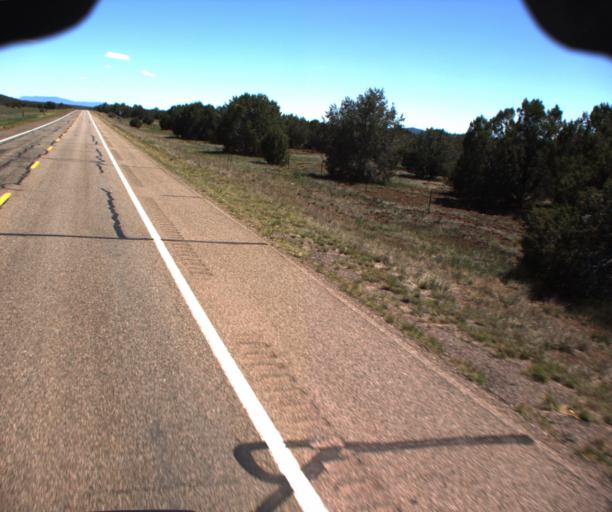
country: US
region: Arizona
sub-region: Yavapai County
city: Paulden
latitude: 35.1558
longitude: -112.4531
